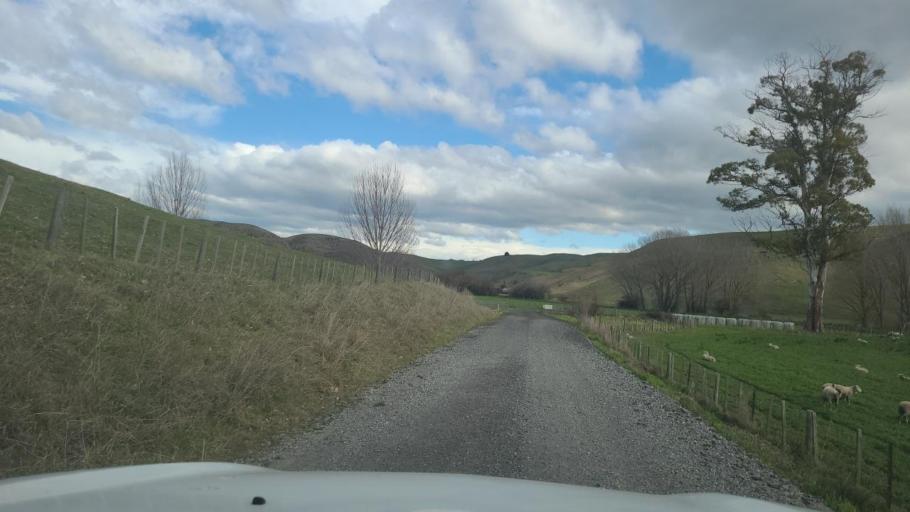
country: NZ
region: Hawke's Bay
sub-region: Hastings District
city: Hastings
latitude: -39.6612
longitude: 176.6446
